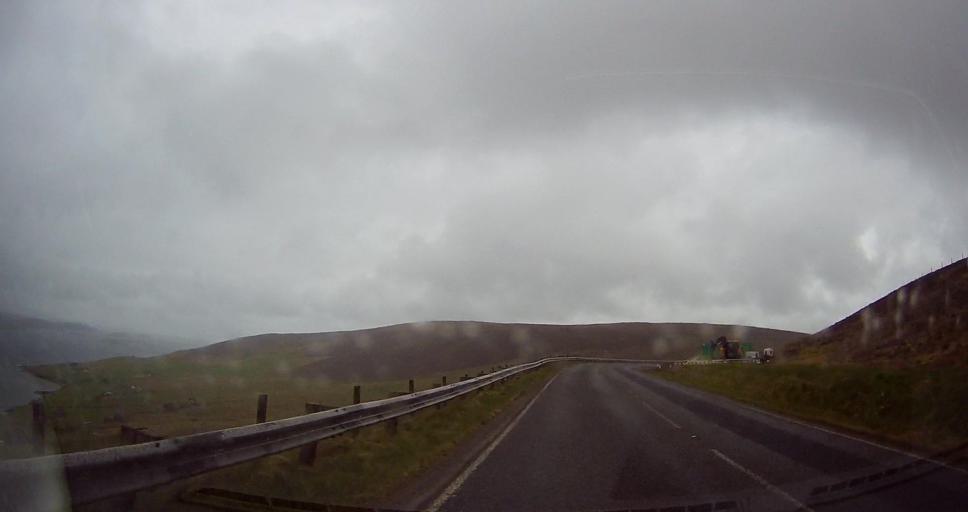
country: GB
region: Scotland
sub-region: Shetland Islands
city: Lerwick
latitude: 60.2372
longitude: -1.3140
